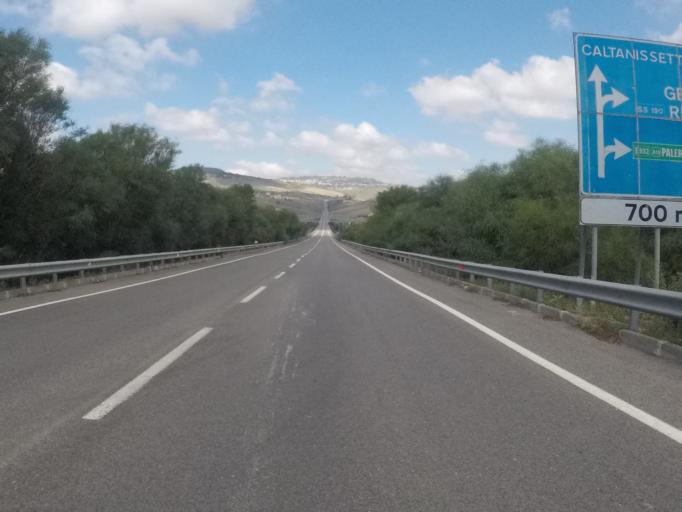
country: IT
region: Sicily
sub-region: Enna
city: Pietraperzia
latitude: 37.4487
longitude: 14.1158
